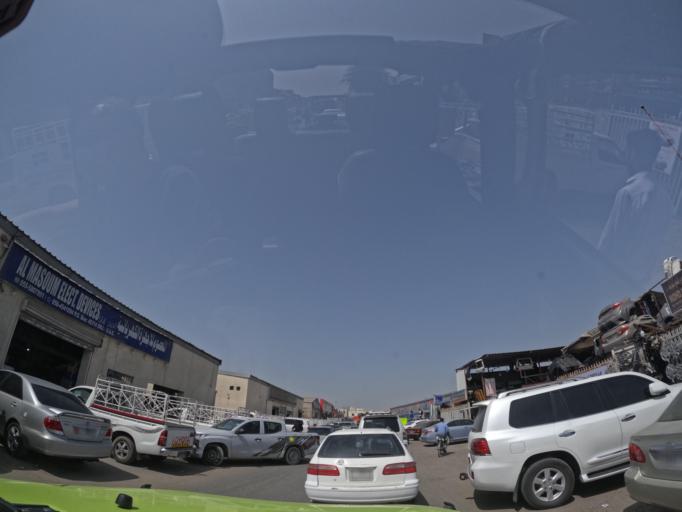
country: AE
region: Ash Shariqah
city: Sharjah
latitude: 25.3161
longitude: 55.4139
